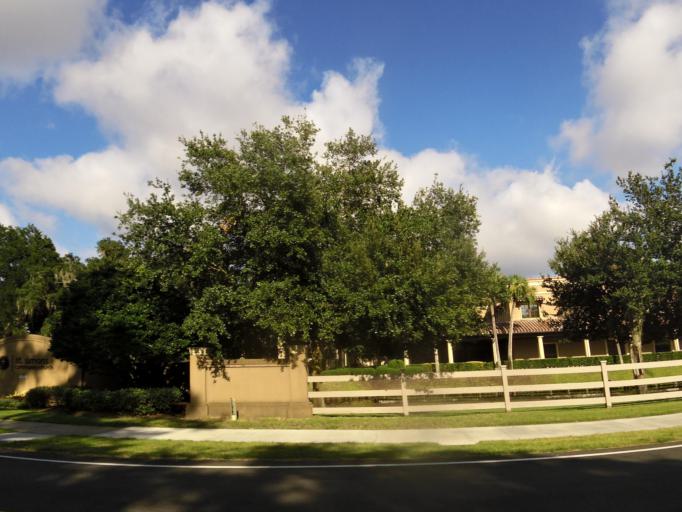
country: US
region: Georgia
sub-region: Glynn County
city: Saint Simons Island
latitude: 31.1769
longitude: -81.3778
